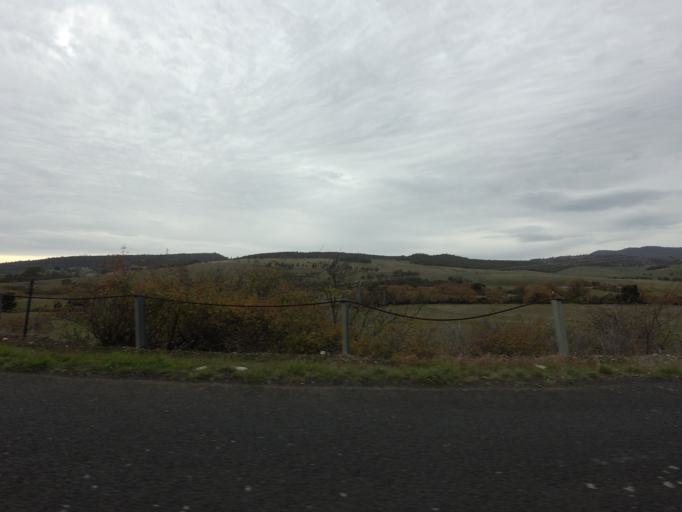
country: AU
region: Tasmania
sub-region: Derwent Valley
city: New Norfolk
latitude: -42.6038
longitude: 147.0767
